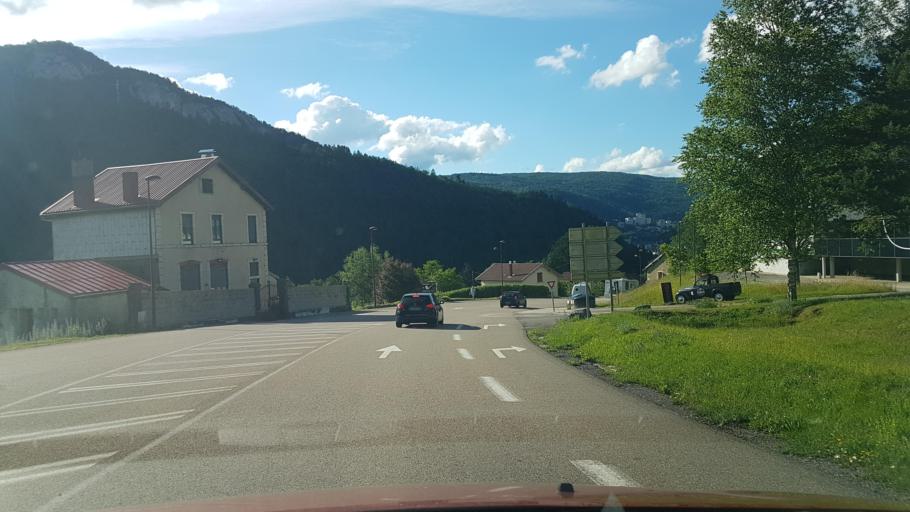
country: FR
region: Franche-Comte
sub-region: Departement du Jura
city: Saint-Claude
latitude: 46.3691
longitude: 5.8753
